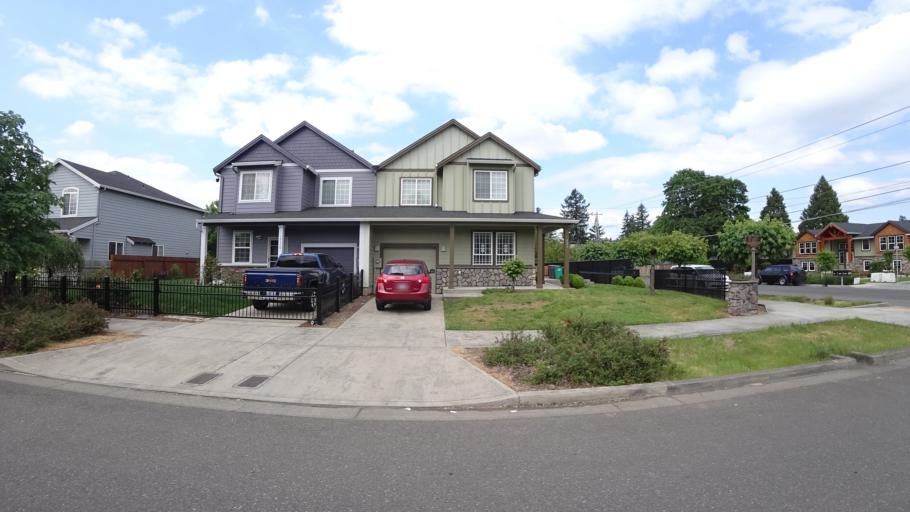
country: US
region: Oregon
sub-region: Multnomah County
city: Gresham
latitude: 45.5062
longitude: -122.4850
